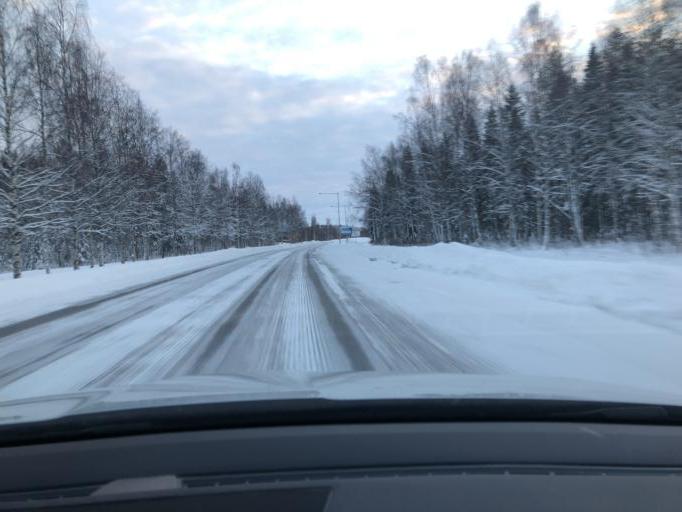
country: SE
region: Norrbotten
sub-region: Lulea Kommun
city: Lulea
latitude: 65.6210
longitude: 22.1275
